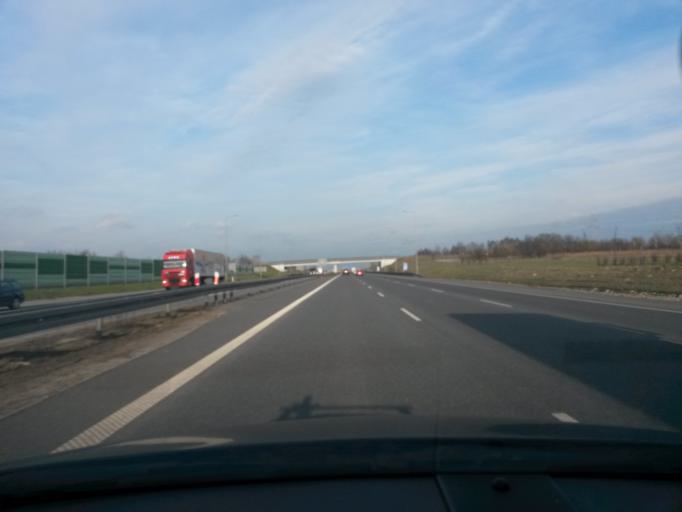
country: PL
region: Lodz Voivodeship
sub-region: Powiat zgierski
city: Strykow
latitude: 51.8897
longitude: 19.6092
